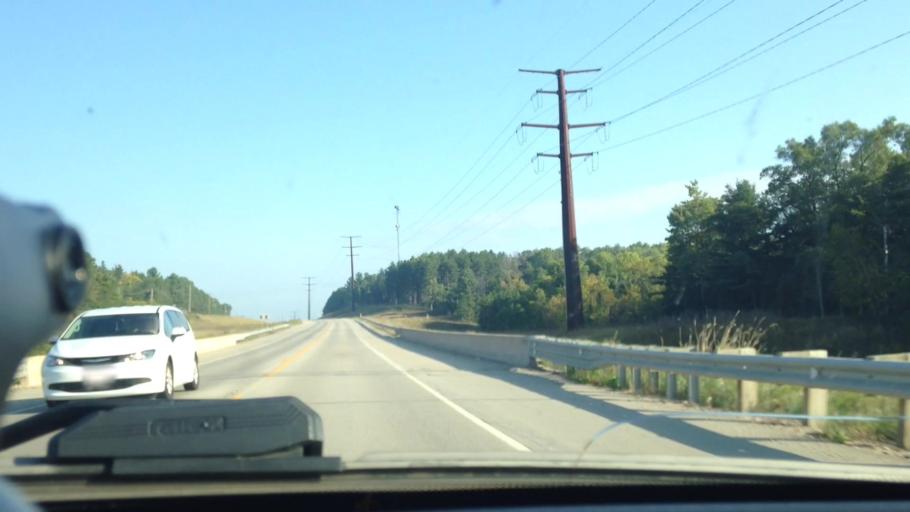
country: US
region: Wisconsin
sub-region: Marinette County
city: Peshtigo
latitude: 45.2085
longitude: -87.9945
